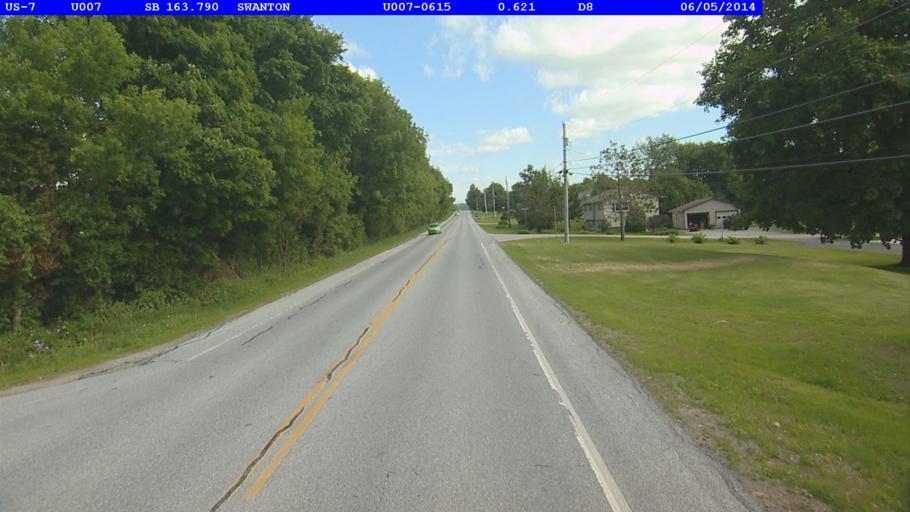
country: US
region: Vermont
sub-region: Franklin County
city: Saint Albans
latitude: 44.8571
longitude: -73.0941
